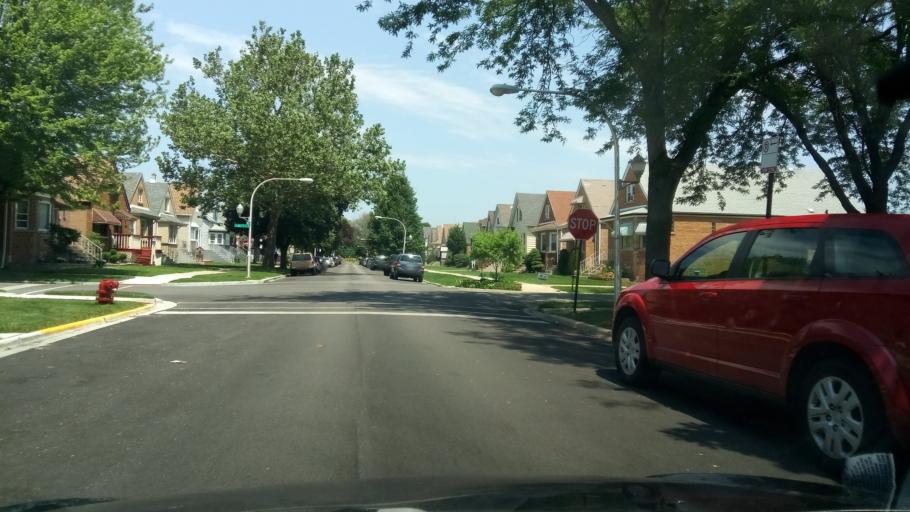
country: US
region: Illinois
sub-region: Cook County
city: Hometown
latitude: 41.7819
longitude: -87.7314
